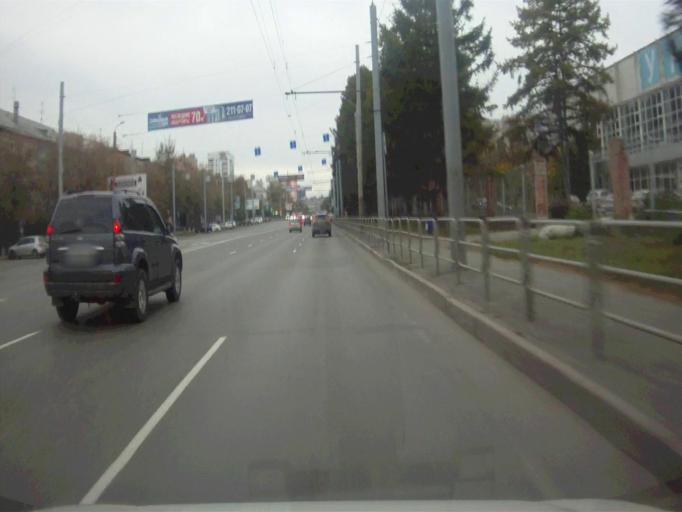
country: RU
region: Chelyabinsk
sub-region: Gorod Chelyabinsk
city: Chelyabinsk
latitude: 55.1650
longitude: 61.3806
